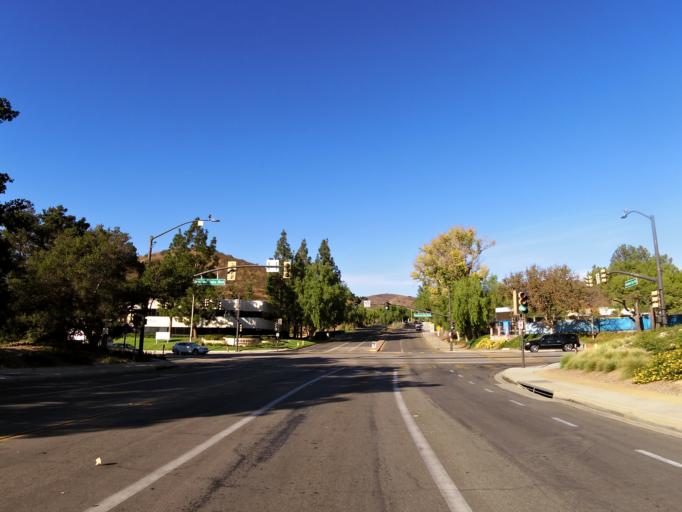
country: US
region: California
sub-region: Los Angeles County
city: Westlake Village
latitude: 34.1583
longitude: -118.8180
